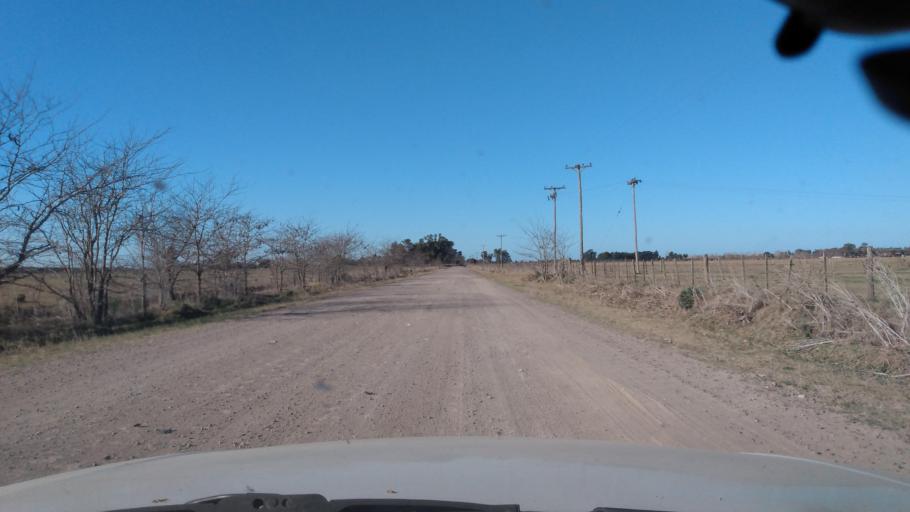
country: AR
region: Buenos Aires
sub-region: Partido de Mercedes
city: Mercedes
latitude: -34.6109
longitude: -59.3173
